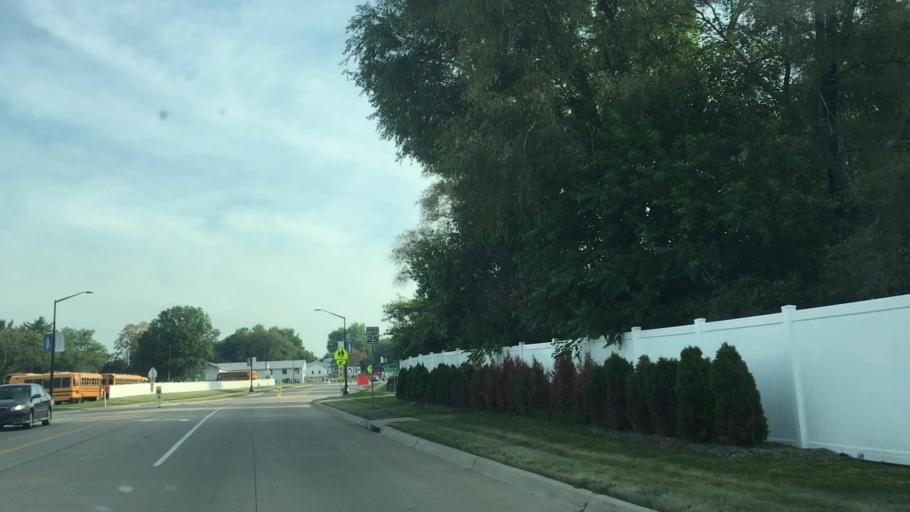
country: US
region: Iowa
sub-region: Johnson County
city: Tiffin
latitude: 41.7053
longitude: -91.6666
